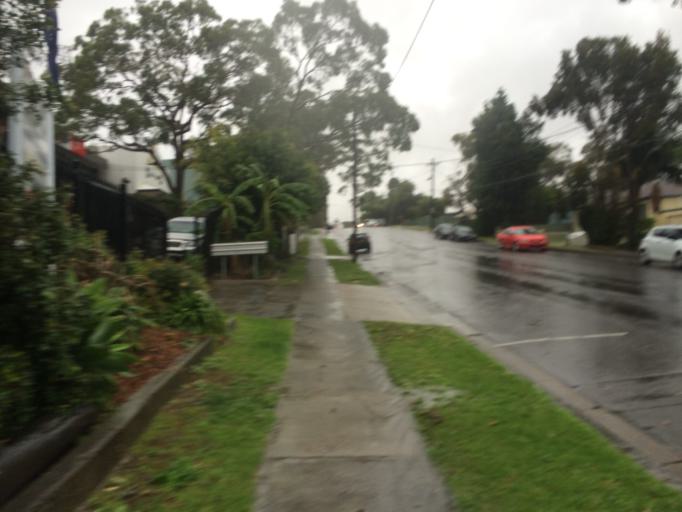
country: AU
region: New South Wales
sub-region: Sutherland Shire
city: Kirrawee
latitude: -34.0262
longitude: 151.0729
